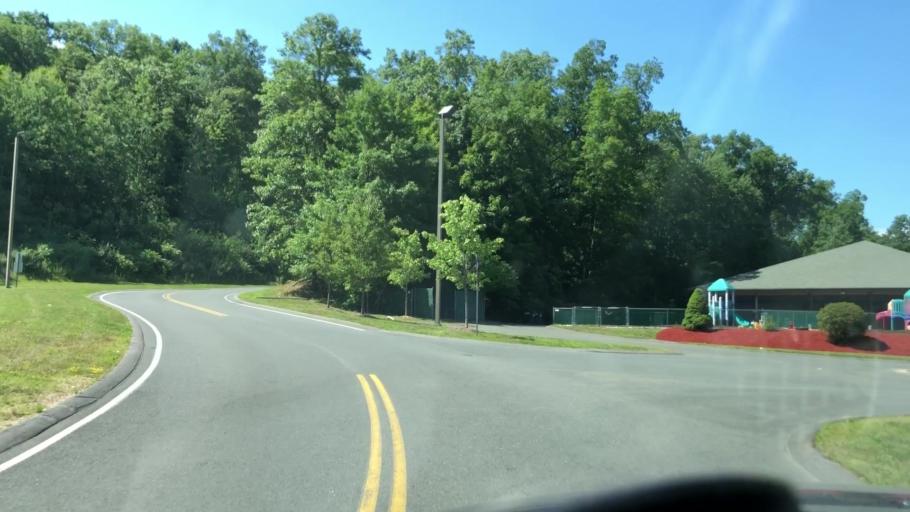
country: US
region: Massachusetts
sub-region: Hampden County
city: Holyoke
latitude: 42.1904
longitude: -72.6529
